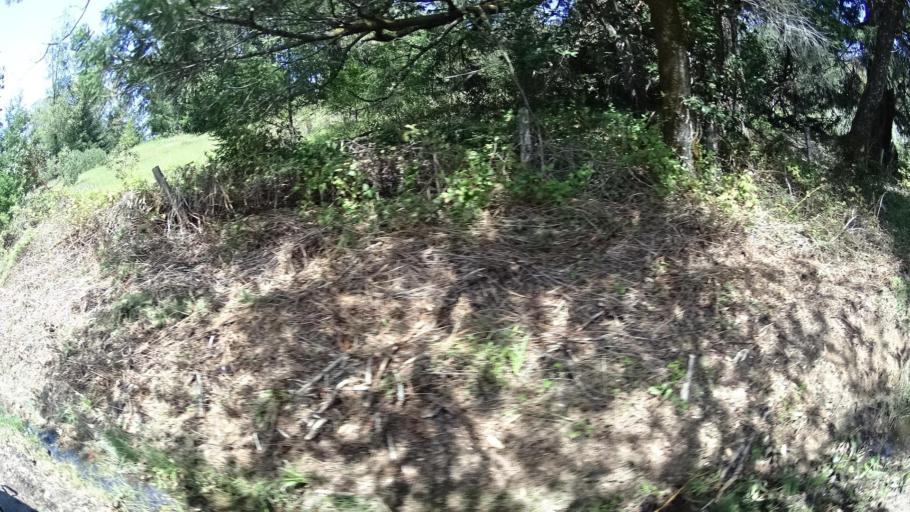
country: US
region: California
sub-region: Humboldt County
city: Redway
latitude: 40.2790
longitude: -123.6409
